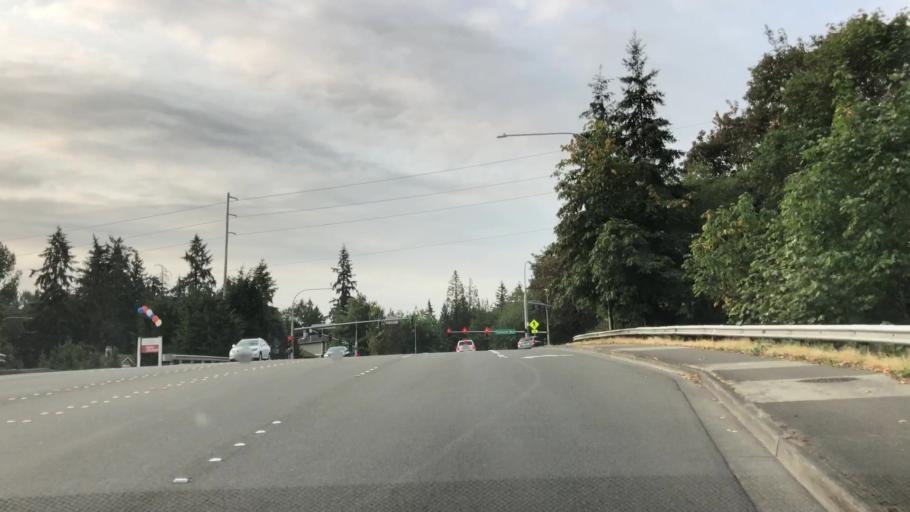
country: US
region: Washington
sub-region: King County
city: Redmond
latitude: 47.6761
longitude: -122.1438
